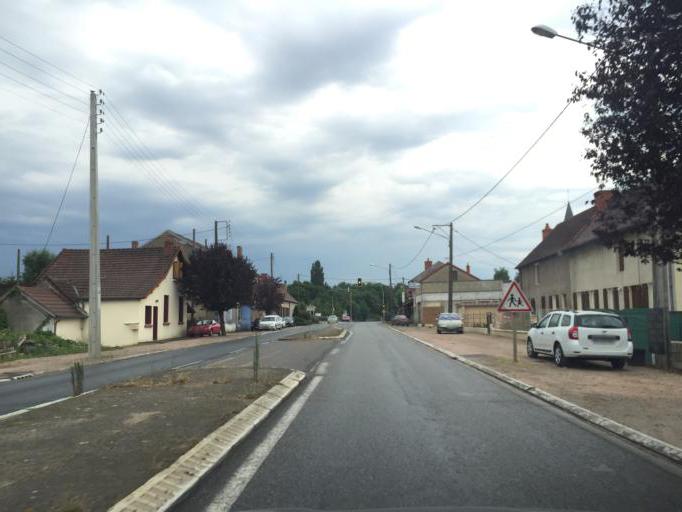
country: FR
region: Auvergne
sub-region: Departement de l'Allier
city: Varennes-sur-Allier
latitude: 46.3519
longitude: 3.3780
